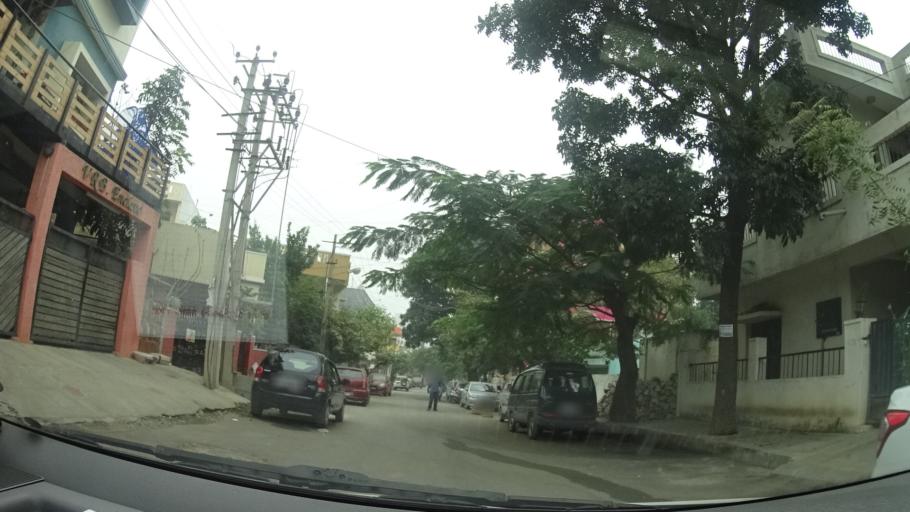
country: IN
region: Karnataka
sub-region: Bangalore Urban
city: Bangalore
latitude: 13.0342
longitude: 77.6318
